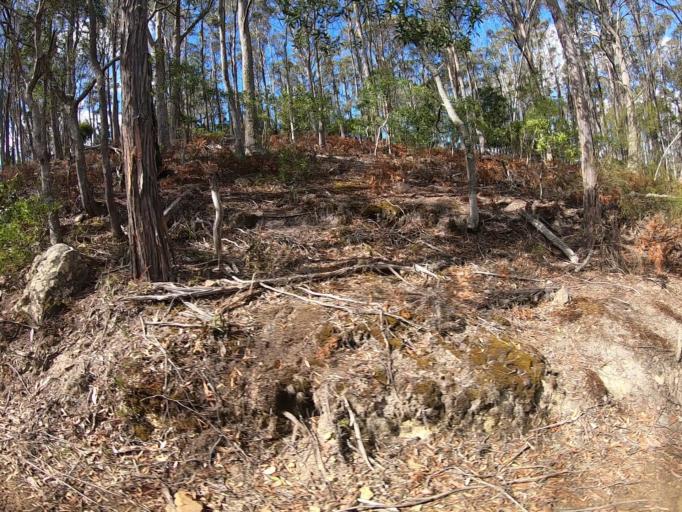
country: AU
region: Tasmania
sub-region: Brighton
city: Bridgewater
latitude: -42.4980
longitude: 147.4223
